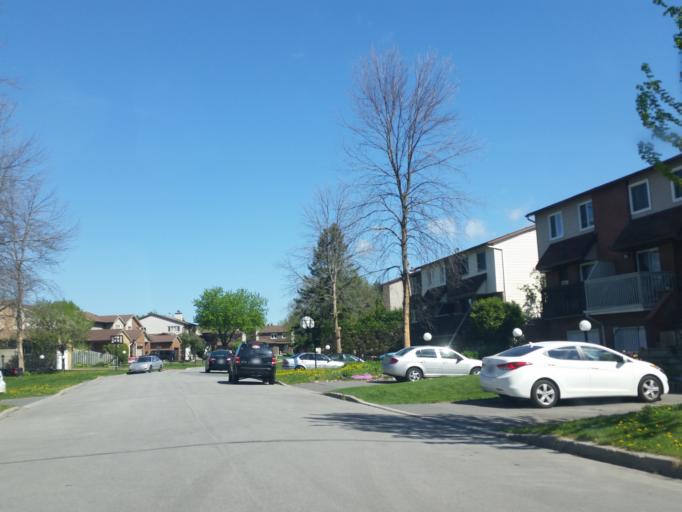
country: CA
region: Ontario
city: Ottawa
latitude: 45.3484
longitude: -75.7136
